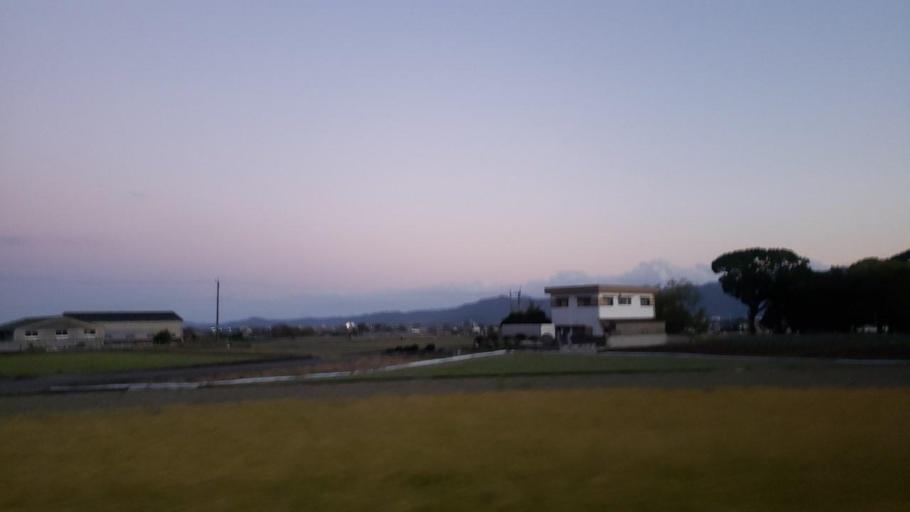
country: JP
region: Tokushima
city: Kamojimacho-jogejima
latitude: 34.1097
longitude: 134.3288
